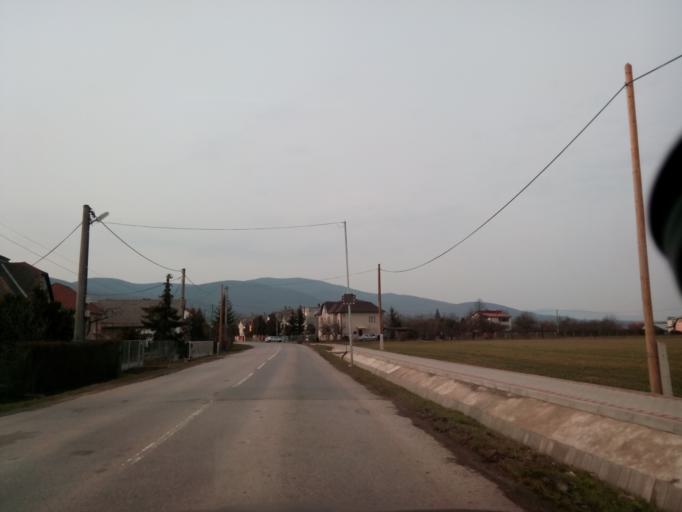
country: SK
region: Kosicky
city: Secovce
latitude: 48.6441
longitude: 21.5777
